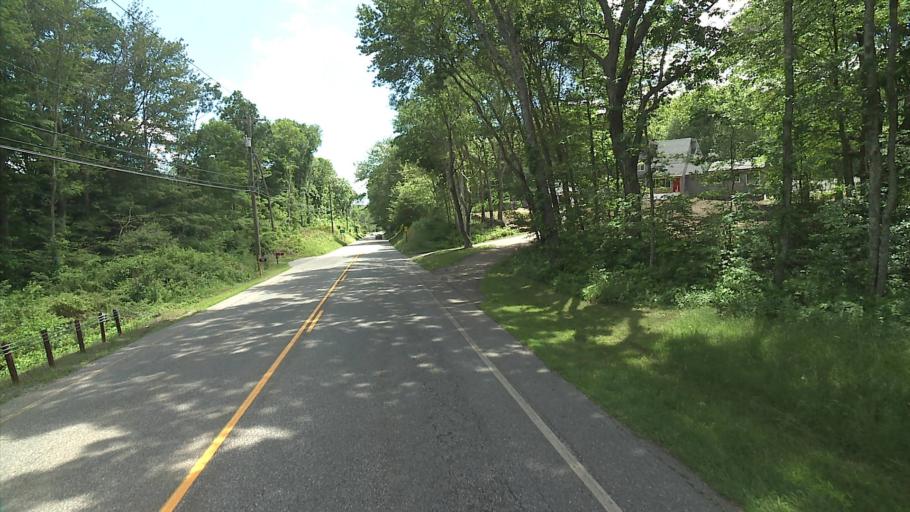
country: US
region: Connecticut
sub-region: New London County
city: Old Mystic
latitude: 41.4205
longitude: -71.8943
